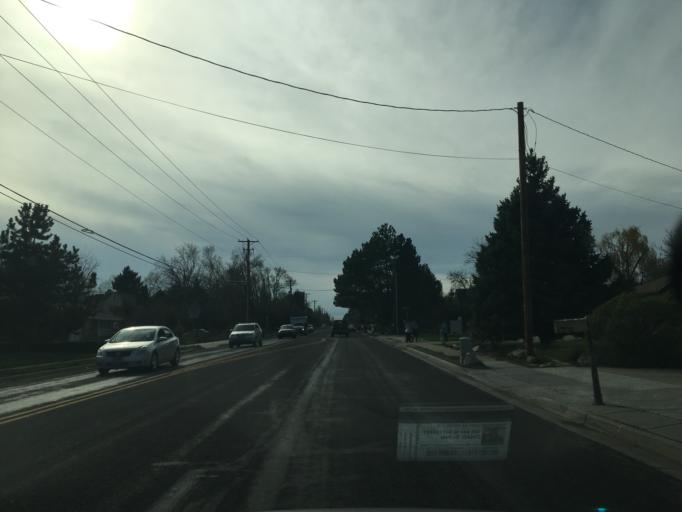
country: US
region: Utah
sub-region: Davis County
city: Layton
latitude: 41.0602
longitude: -111.9762
